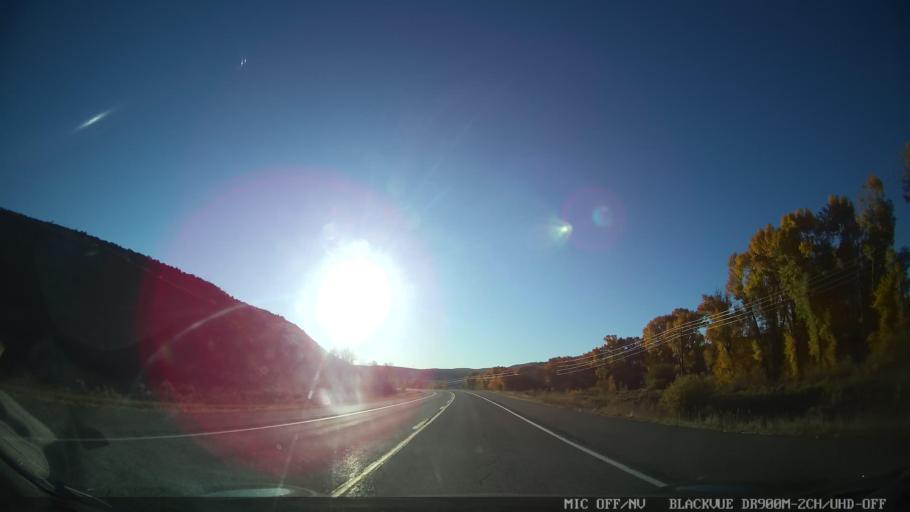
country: US
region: Colorado
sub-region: Grand County
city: Kremmling
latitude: 40.0637
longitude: -106.2525
